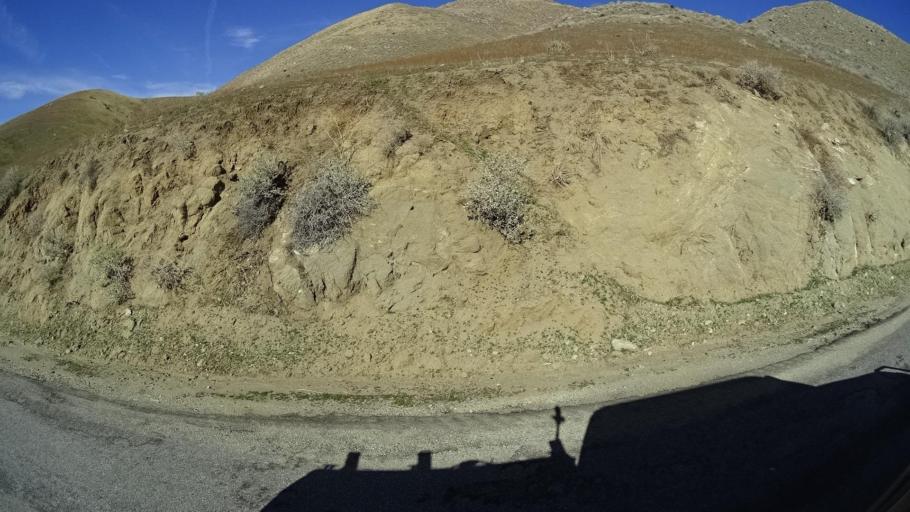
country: US
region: California
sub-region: Kern County
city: Arvin
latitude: 35.4217
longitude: -118.7421
